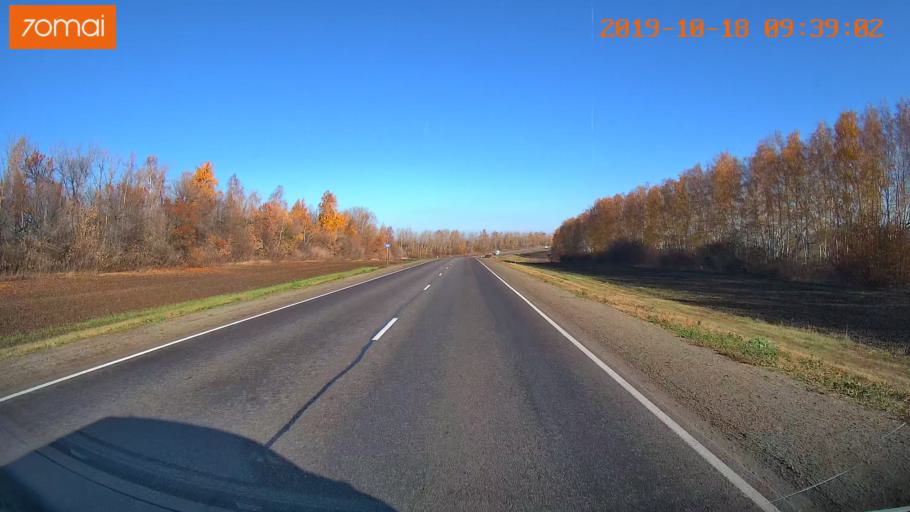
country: RU
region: Tula
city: Yefremov
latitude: 53.2471
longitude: 38.1346
